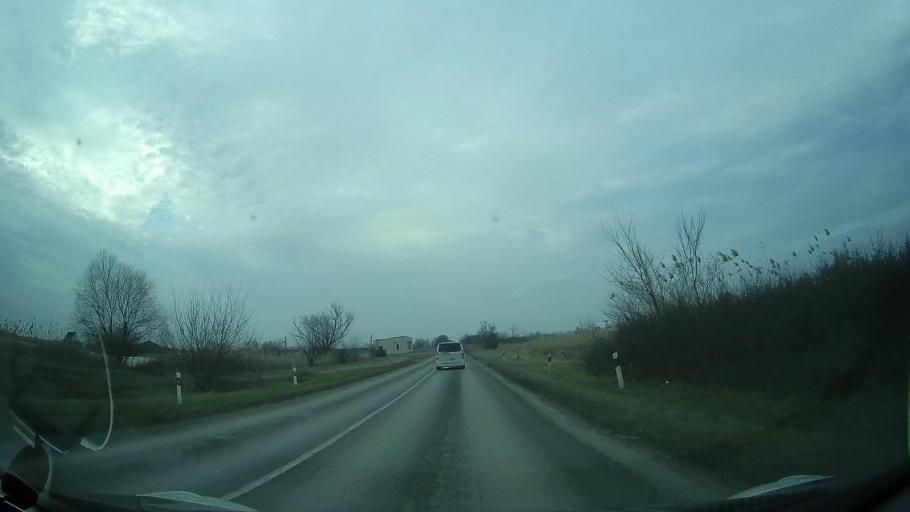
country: RU
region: Rostov
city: Ol'ginskaya
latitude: 47.2118
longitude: 39.9169
